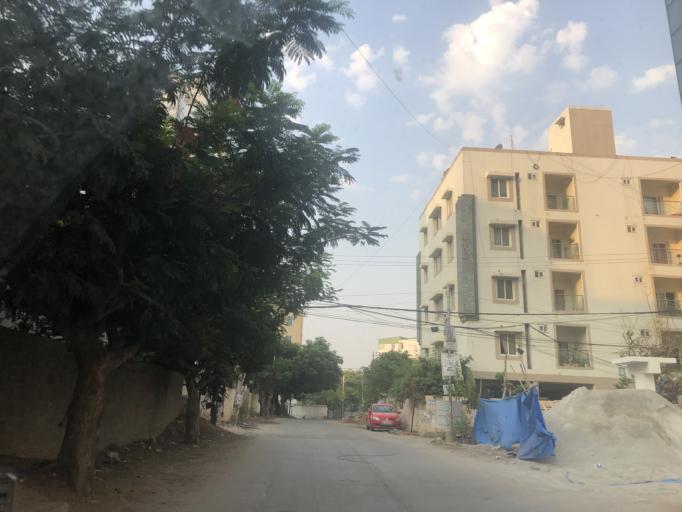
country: IN
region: Telangana
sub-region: Rangareddi
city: Kukatpalli
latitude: 17.4430
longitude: 78.3984
